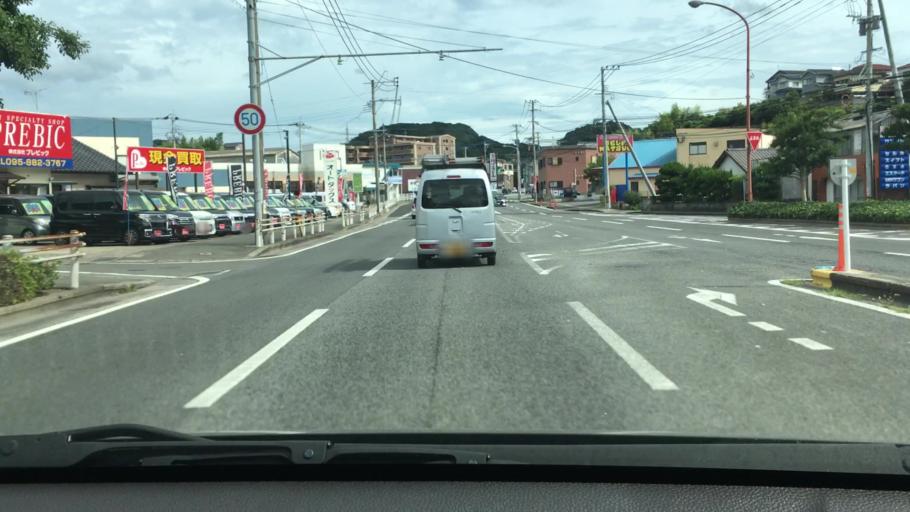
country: JP
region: Nagasaki
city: Togitsu
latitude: 32.8413
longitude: 129.8371
